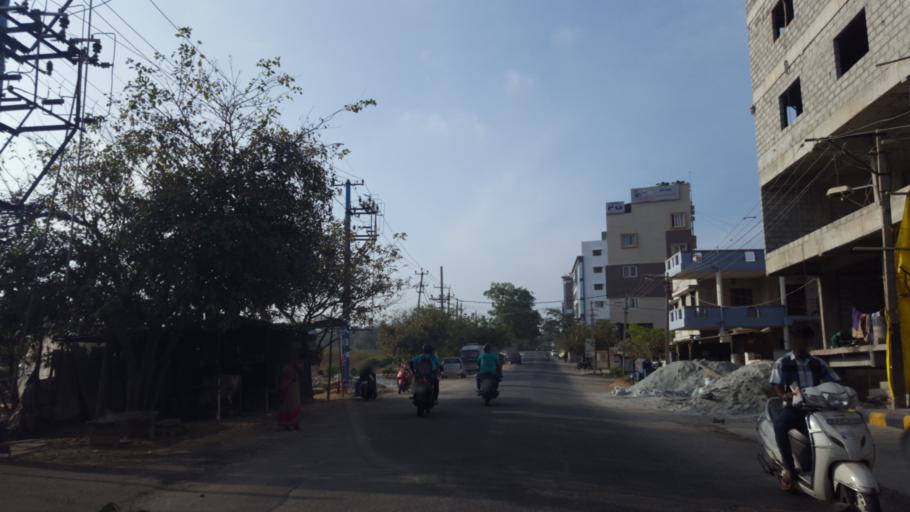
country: IN
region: Karnataka
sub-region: Bangalore Urban
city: Bangalore
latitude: 12.9150
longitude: 77.5006
